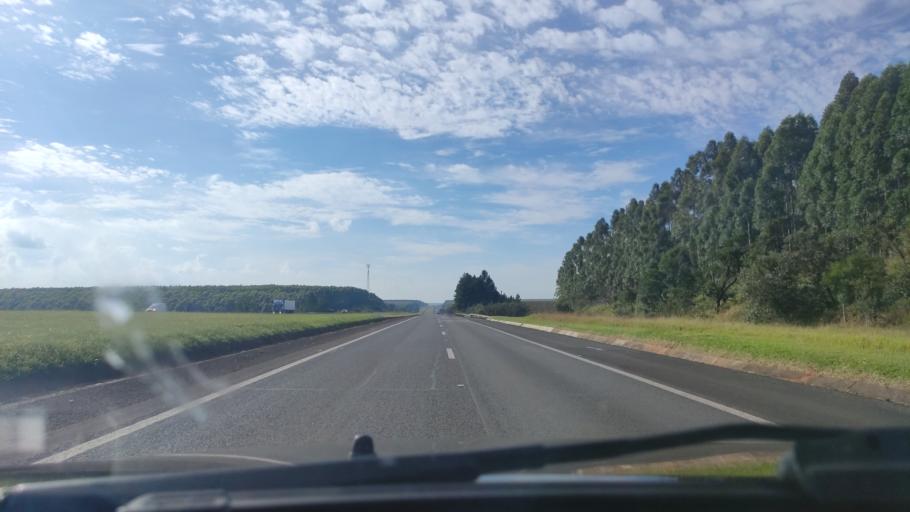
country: BR
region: Sao Paulo
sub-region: Itatinga
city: Itatinga
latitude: -23.0177
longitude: -48.6833
